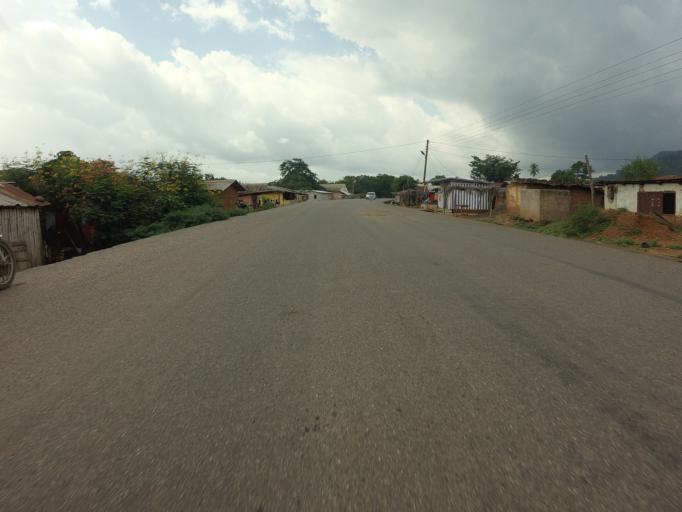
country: GH
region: Volta
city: Kpandu
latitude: 6.8989
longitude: 0.4335
